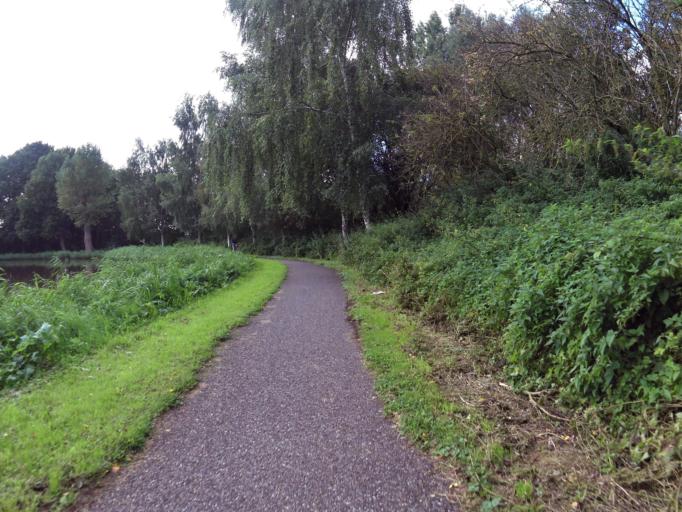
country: NL
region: Utrecht
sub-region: Stichtse Vecht
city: Maarssen
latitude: 52.1625
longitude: 5.0308
